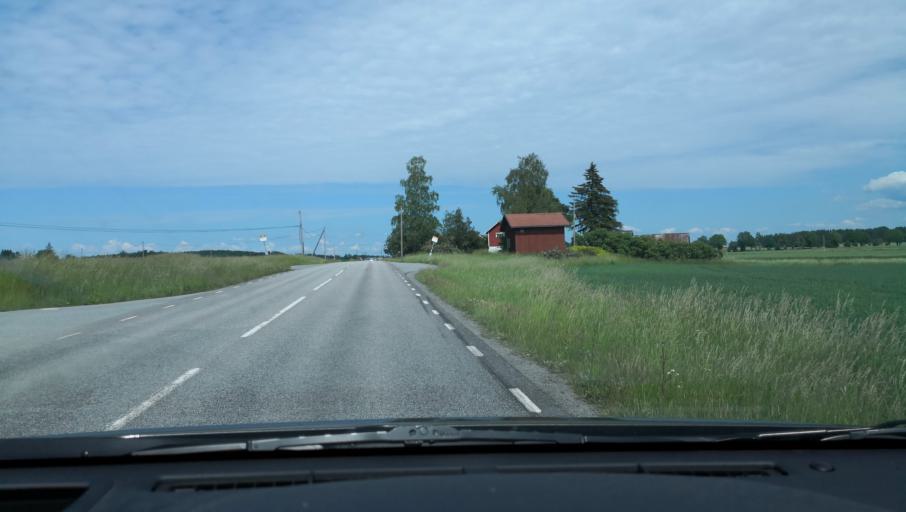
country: SE
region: Stockholm
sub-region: Sigtuna Kommun
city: Sigtuna
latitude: 59.6642
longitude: 17.6910
